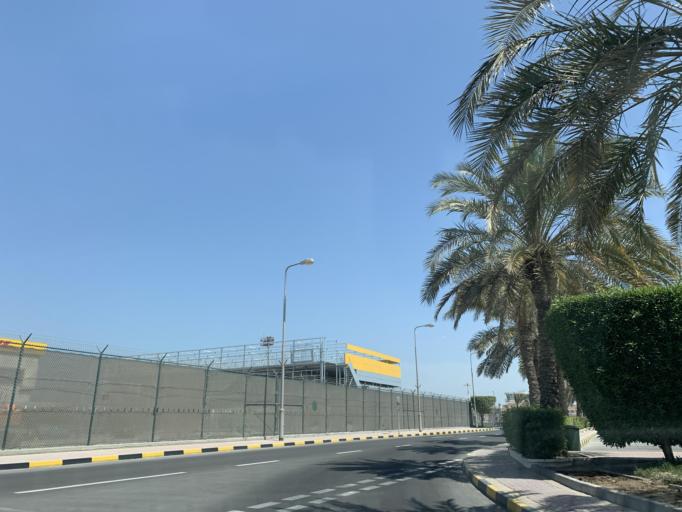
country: BH
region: Muharraq
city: Al Muharraq
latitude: 26.2713
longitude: 50.6226
